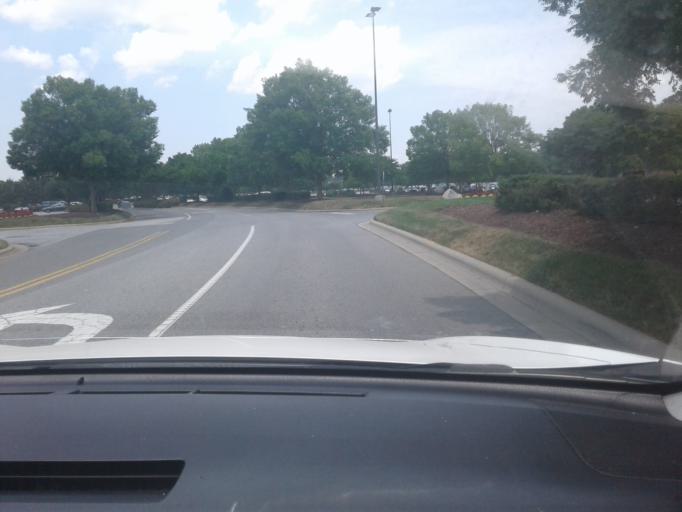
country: US
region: North Carolina
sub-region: Wake County
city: Garner
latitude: 35.6911
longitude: -78.5801
